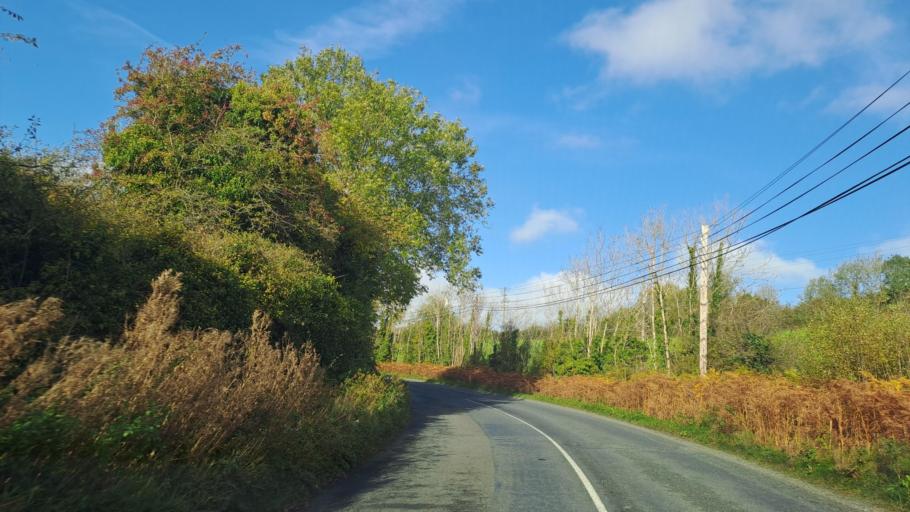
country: IE
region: Ulster
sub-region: An Cabhan
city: Bailieborough
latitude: 54.0137
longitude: -6.9257
